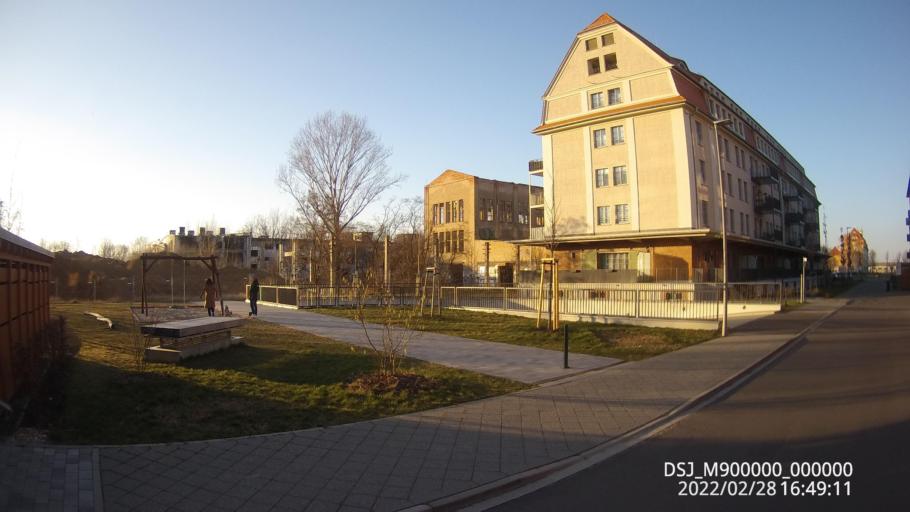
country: DE
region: Saxony
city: Leipzig
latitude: 51.3722
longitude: 12.3522
